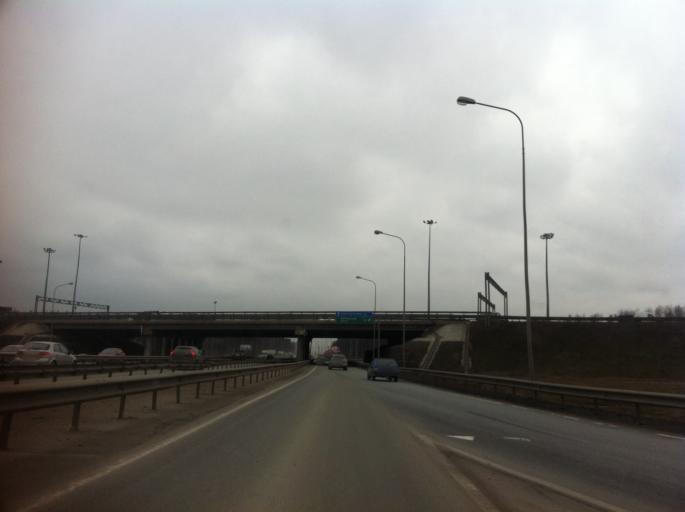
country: RU
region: St.-Petersburg
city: Krasnogvargeisky
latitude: 59.9463
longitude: 30.5434
